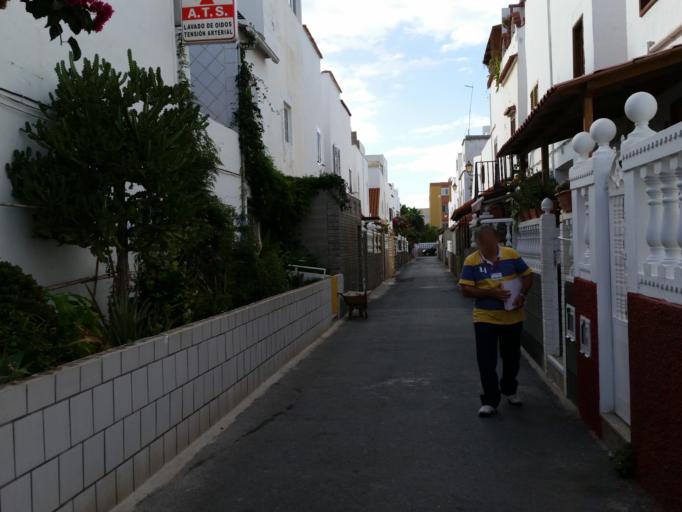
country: ES
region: Canary Islands
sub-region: Provincia de Las Palmas
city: Playa del Ingles
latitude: 27.7671
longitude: -15.5768
